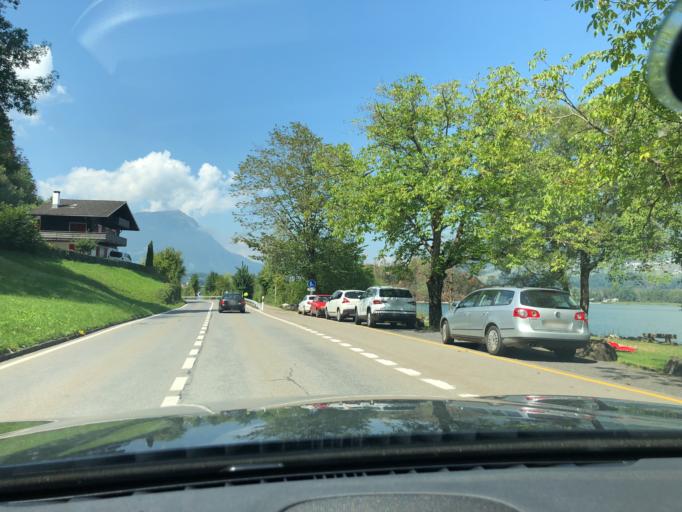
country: CH
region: Schwyz
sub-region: Bezirk Schwyz
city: Steinen
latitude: 47.0300
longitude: 8.6023
